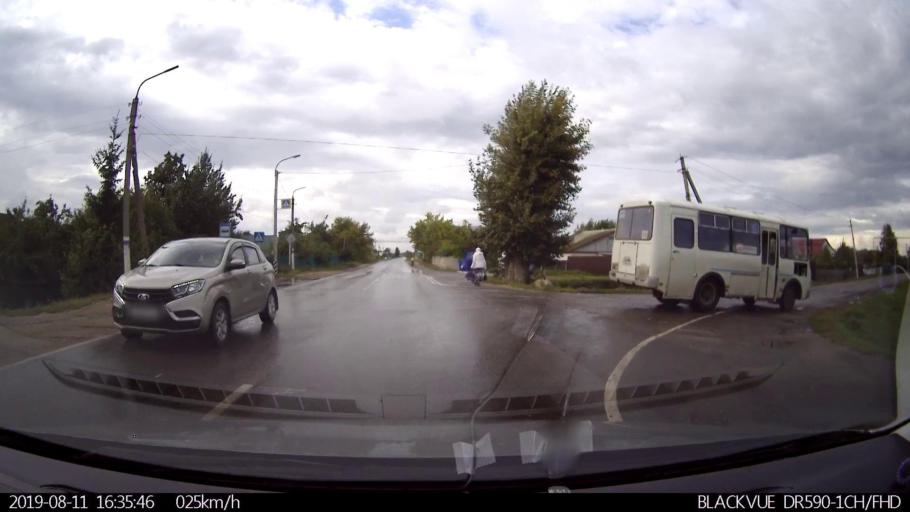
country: RU
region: Ulyanovsk
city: Mayna
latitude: 54.1160
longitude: 47.6146
